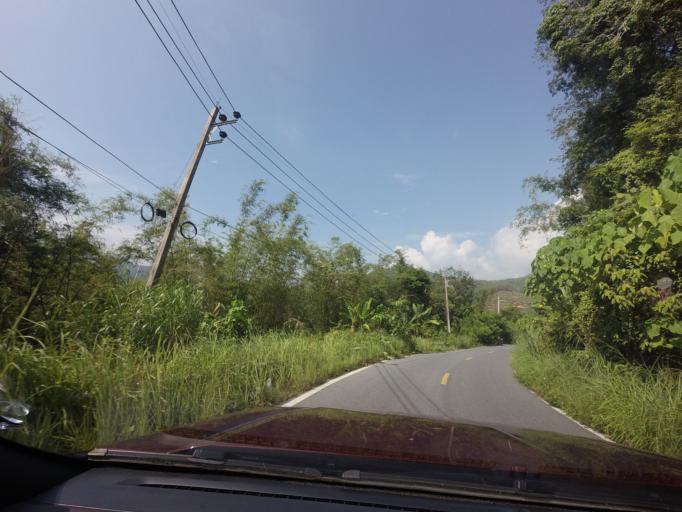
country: TH
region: Yala
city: Than To
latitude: 5.9869
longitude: 101.2008
